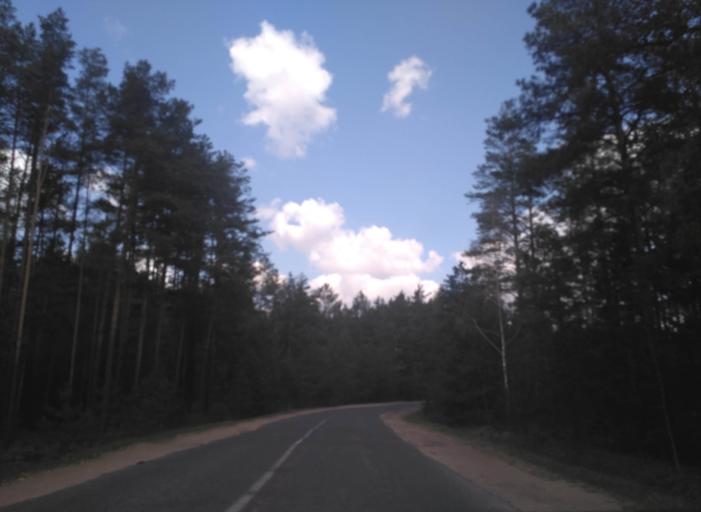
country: BY
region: Minsk
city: Radashkovichy
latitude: 54.1714
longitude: 27.2442
